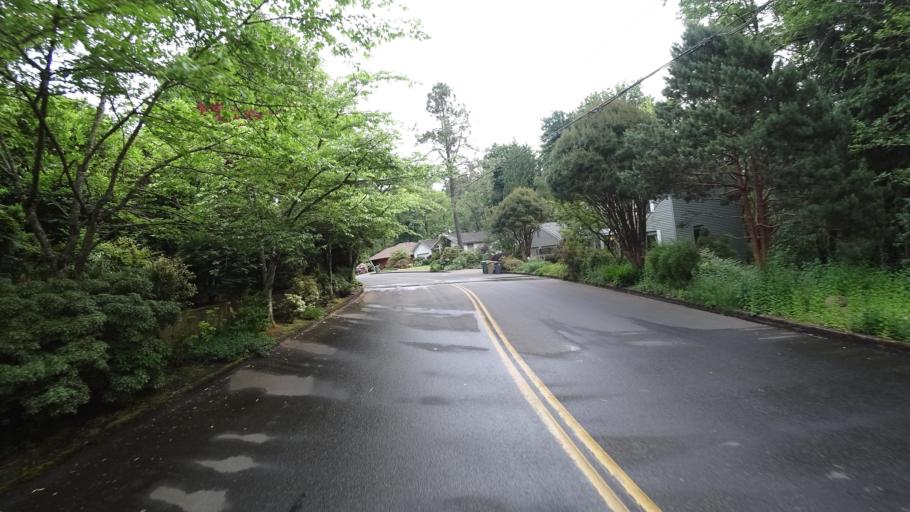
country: US
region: Oregon
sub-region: Clackamas County
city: Lake Oswego
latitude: 45.4275
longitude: -122.6807
